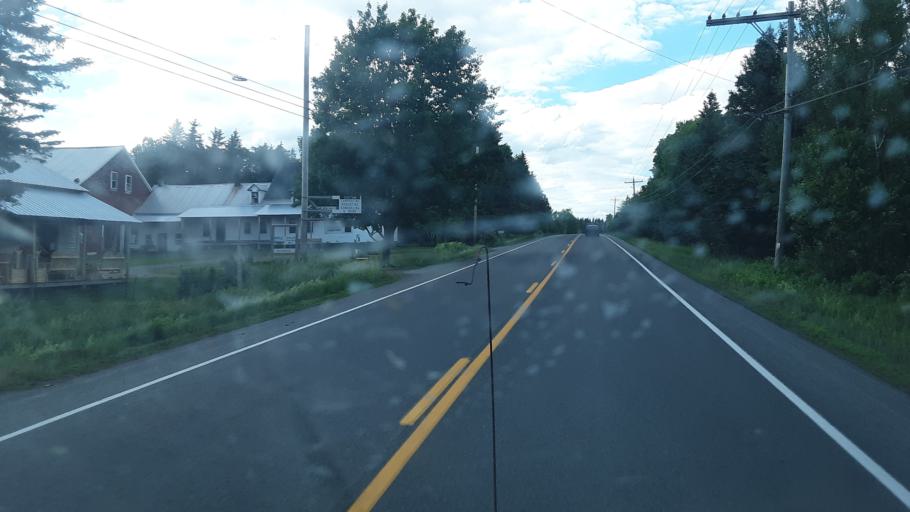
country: US
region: Maine
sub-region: Penobscot County
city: Patten
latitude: 45.9376
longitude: -68.4502
